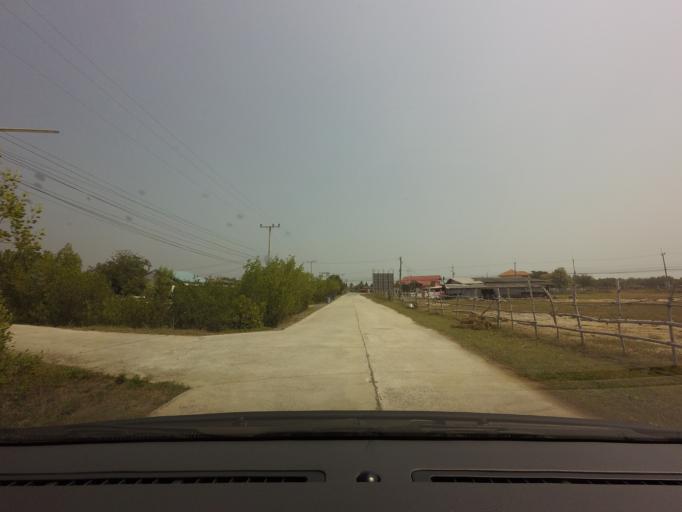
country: TH
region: Prachuap Khiri Khan
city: Kui Buri
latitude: 12.1359
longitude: 99.9627
